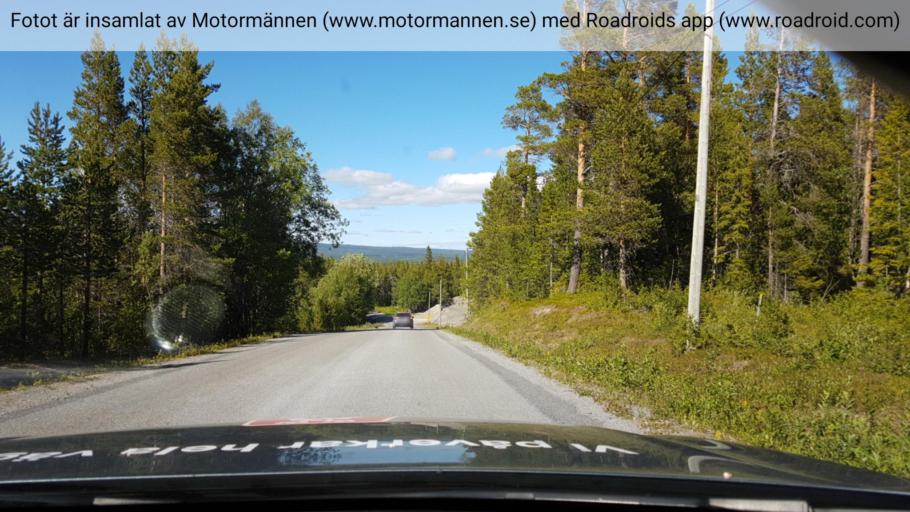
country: SE
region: Jaemtland
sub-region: Are Kommun
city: Are
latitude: 63.1666
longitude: 13.0771
